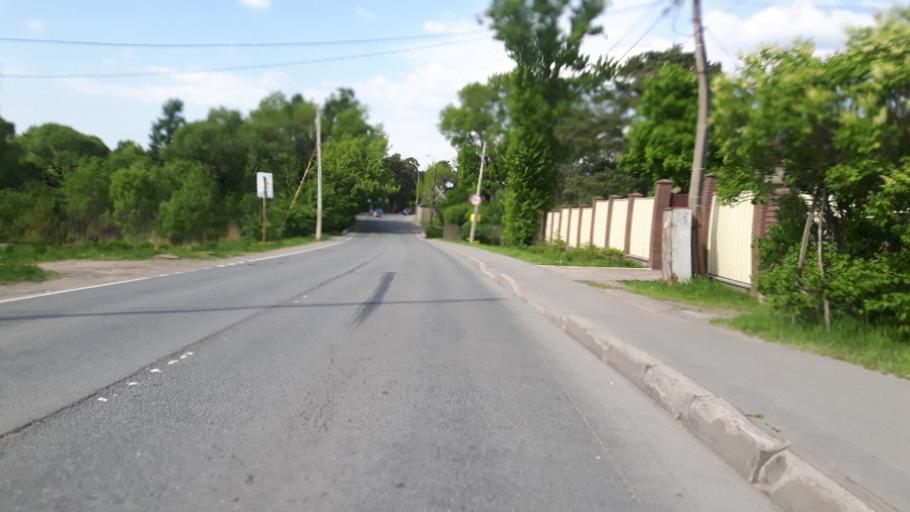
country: RU
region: Leningrad
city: Gorskaya
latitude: 60.0436
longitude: 29.9776
